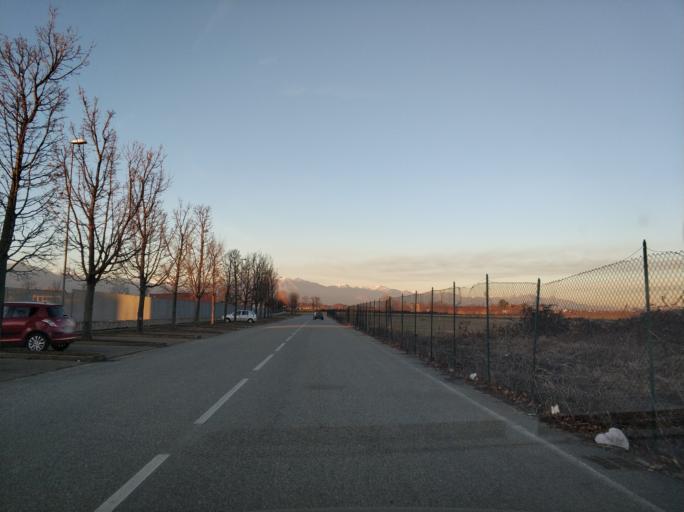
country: IT
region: Piedmont
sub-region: Provincia di Torino
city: San Maurizio
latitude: 45.2056
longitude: 7.6435
